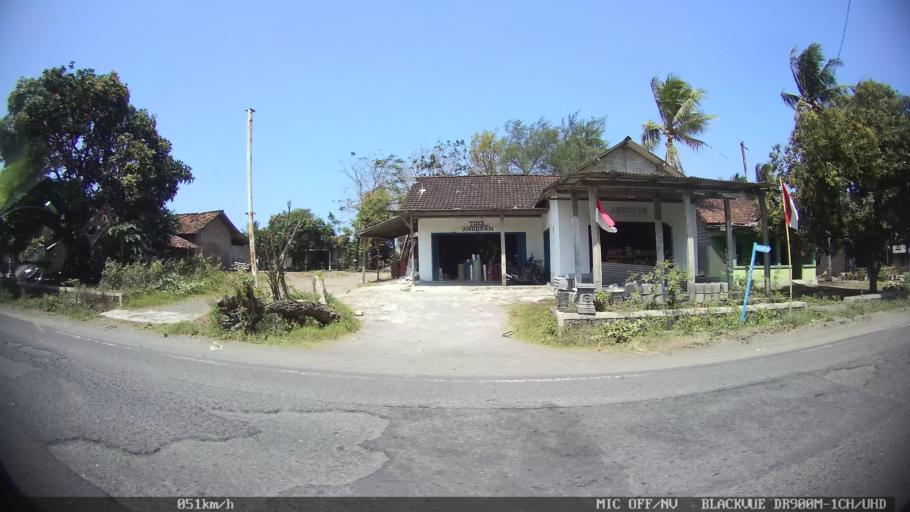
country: ID
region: Daerah Istimewa Yogyakarta
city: Srandakan
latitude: -7.9142
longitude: 110.0957
